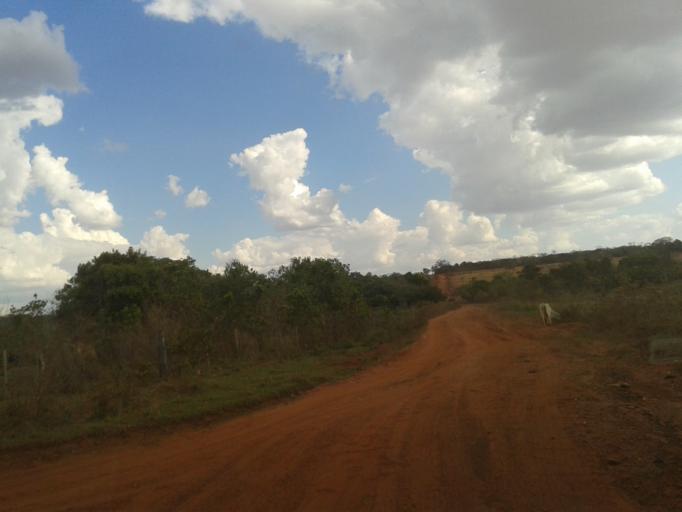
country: BR
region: Minas Gerais
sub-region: Santa Vitoria
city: Santa Vitoria
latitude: -19.2451
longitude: -49.9766
